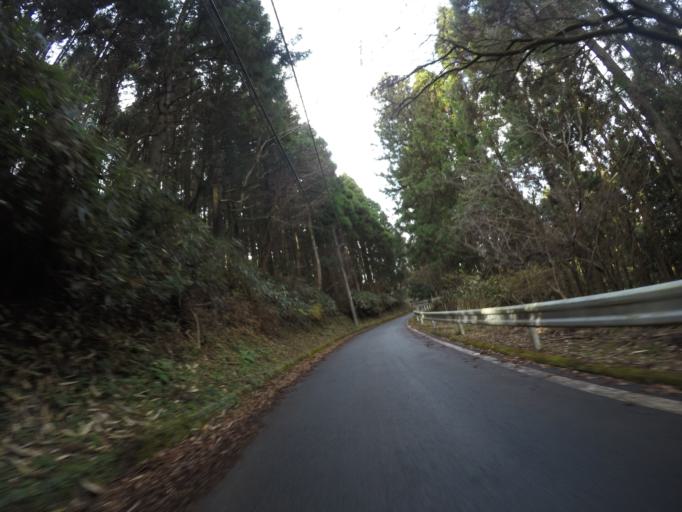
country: JP
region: Shizuoka
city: Heda
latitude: 34.8740
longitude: 138.8550
